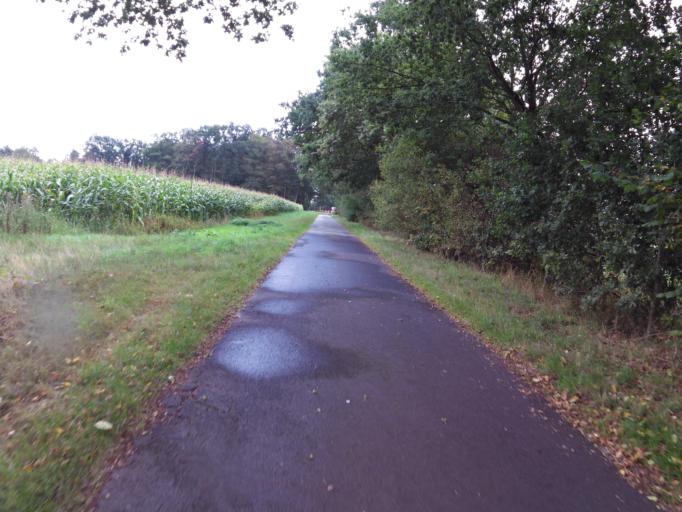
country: DE
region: Lower Saxony
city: Hamersen
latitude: 53.2607
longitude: 9.4782
